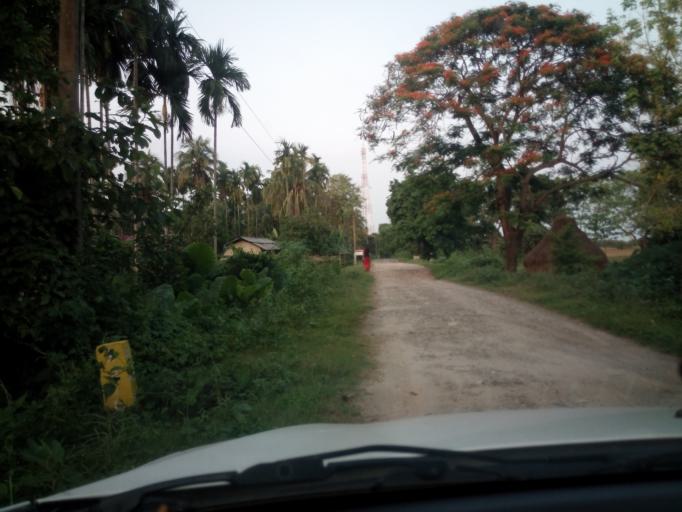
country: IN
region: Assam
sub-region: Udalguri
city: Udalguri
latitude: 26.6828
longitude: 92.1098
